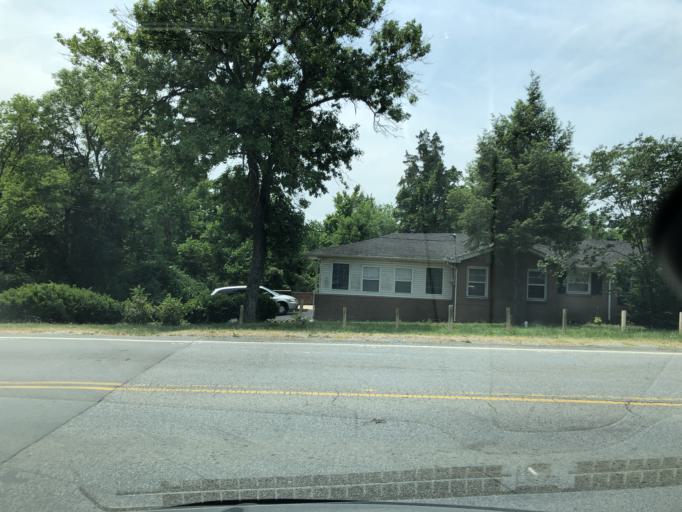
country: US
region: Tennessee
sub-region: Davidson County
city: Oak Hill
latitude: 36.0665
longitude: -86.6813
